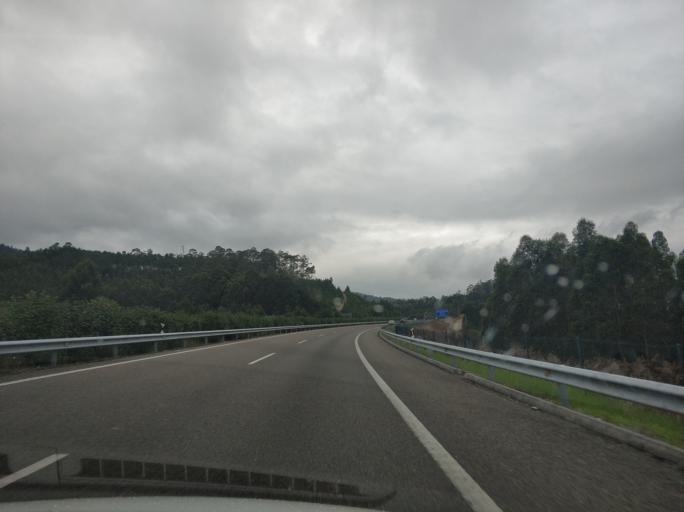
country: ES
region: Galicia
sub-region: Provincia de Lugo
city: Ribadeo
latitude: 43.5370
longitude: -7.0842
